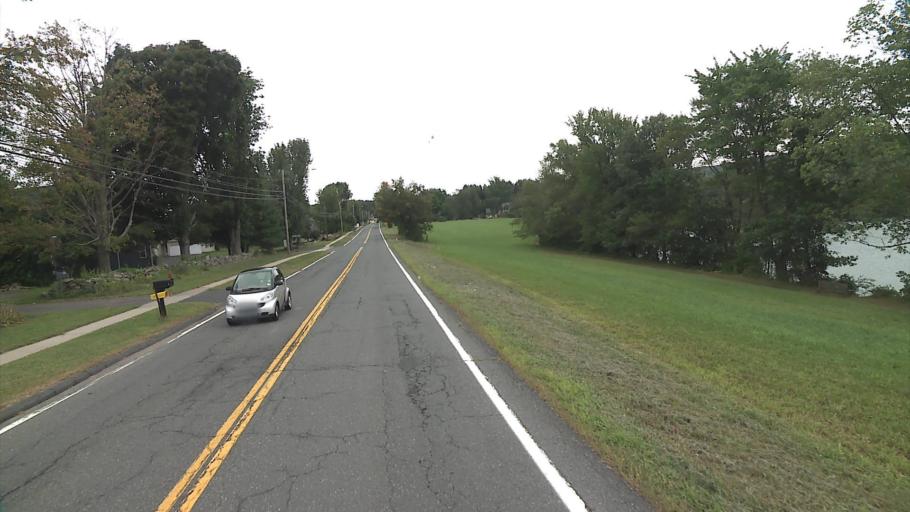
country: US
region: Connecticut
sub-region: Hartford County
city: Manchester
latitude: 41.8006
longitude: -72.4722
